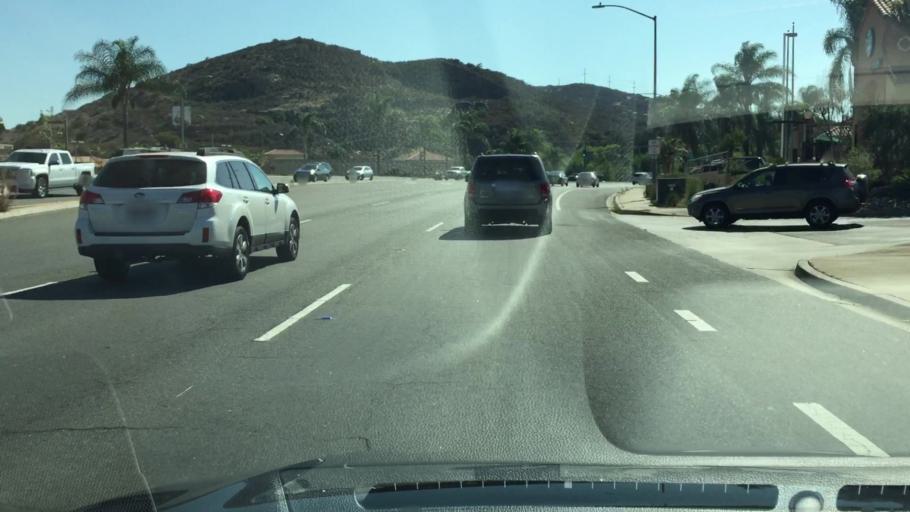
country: US
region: California
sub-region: San Diego County
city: Rancho San Diego
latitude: 32.7402
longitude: -116.9403
